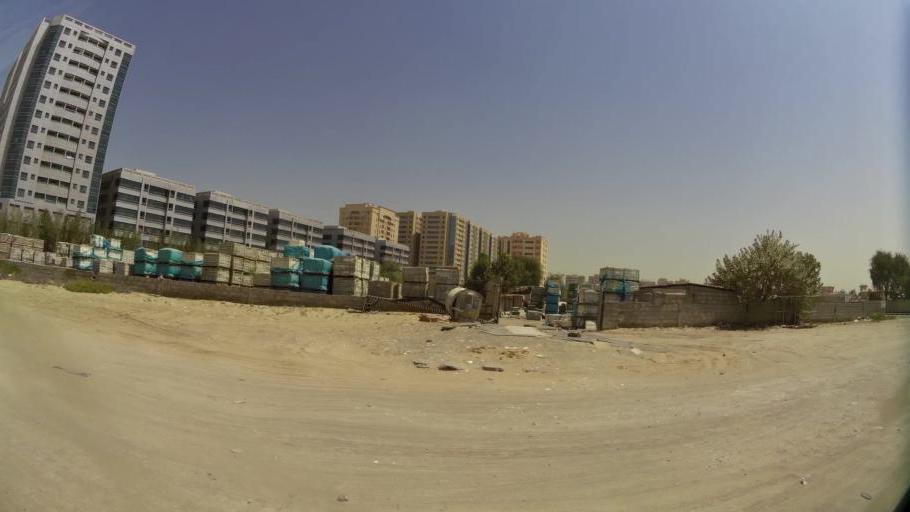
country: AE
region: Ajman
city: Ajman
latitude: 25.4016
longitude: 55.5079
